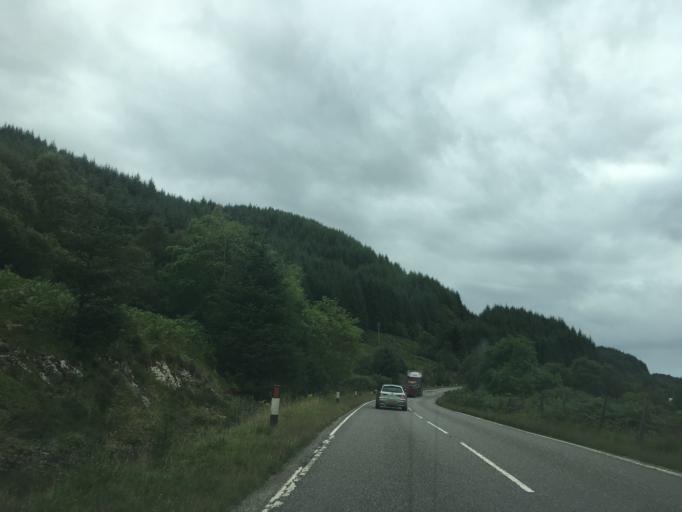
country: GB
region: Scotland
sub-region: Argyll and Bute
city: Oban
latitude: 56.2909
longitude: -5.4701
